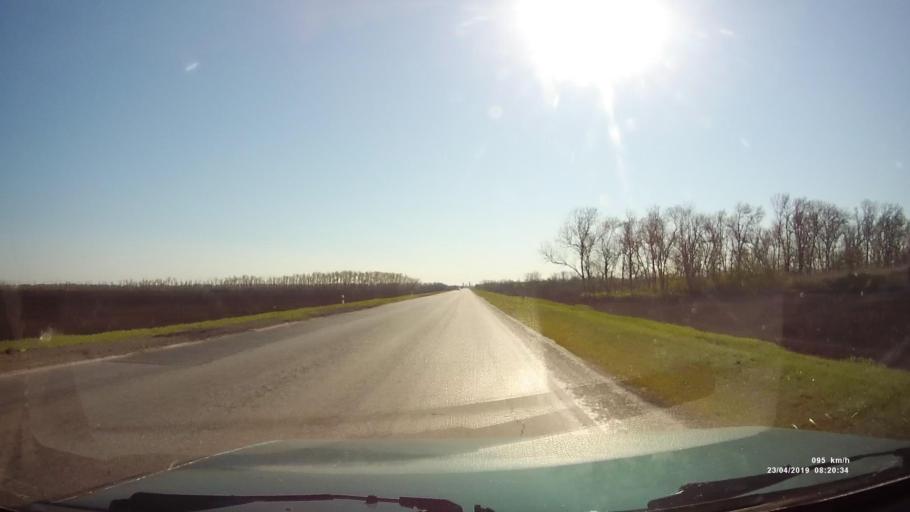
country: RU
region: Rostov
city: Tselina
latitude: 46.5363
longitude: 40.8715
